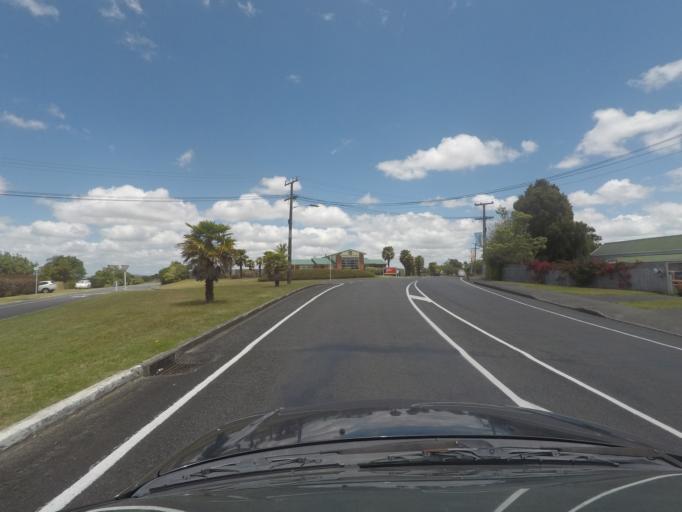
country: NZ
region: Northland
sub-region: Whangarei
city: Whangarei
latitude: -35.7646
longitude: 174.3672
